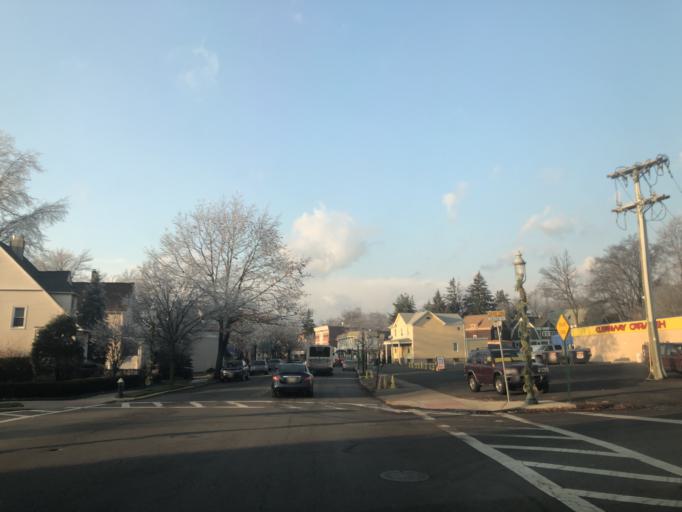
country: US
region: New Jersey
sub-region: Essex County
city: South Orange
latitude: 40.7391
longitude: -74.2524
